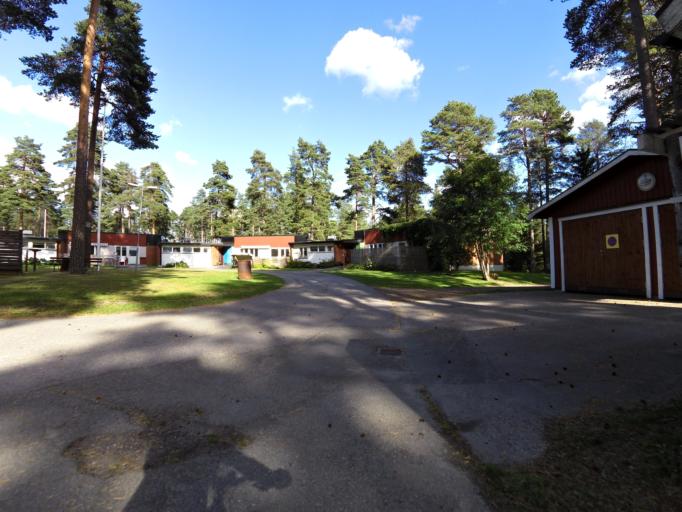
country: SE
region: Gaevleborg
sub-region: Gavle Kommun
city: Gavle
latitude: 60.7082
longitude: 17.1693
